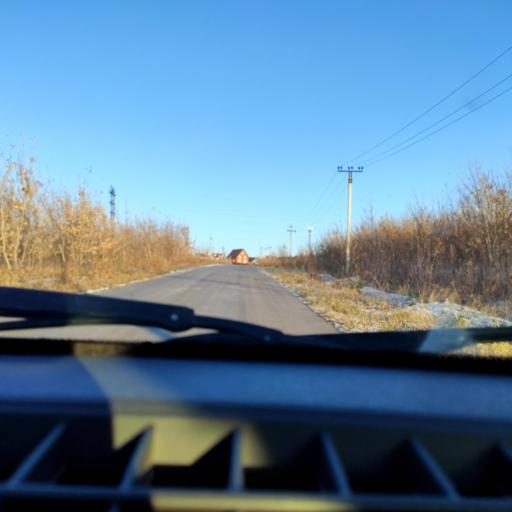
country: RU
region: Bashkortostan
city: Avdon
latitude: 54.6534
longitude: 55.7518
